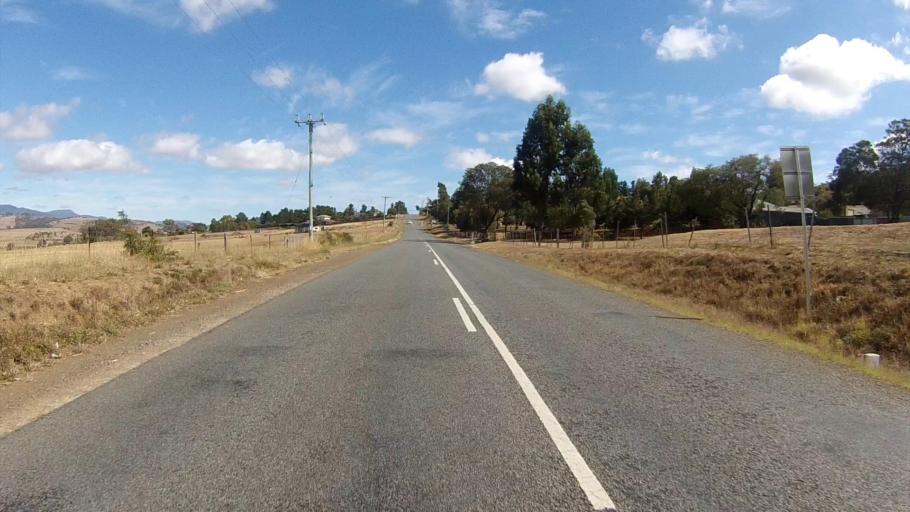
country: AU
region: Tasmania
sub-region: Brighton
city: Bridgewater
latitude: -42.7185
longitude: 147.2776
